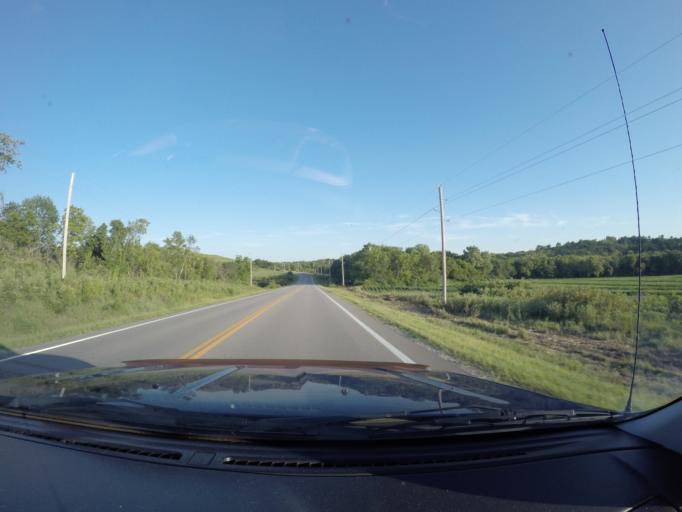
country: US
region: Kansas
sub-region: Pottawatomie County
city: Wamego
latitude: 39.1304
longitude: -96.2997
